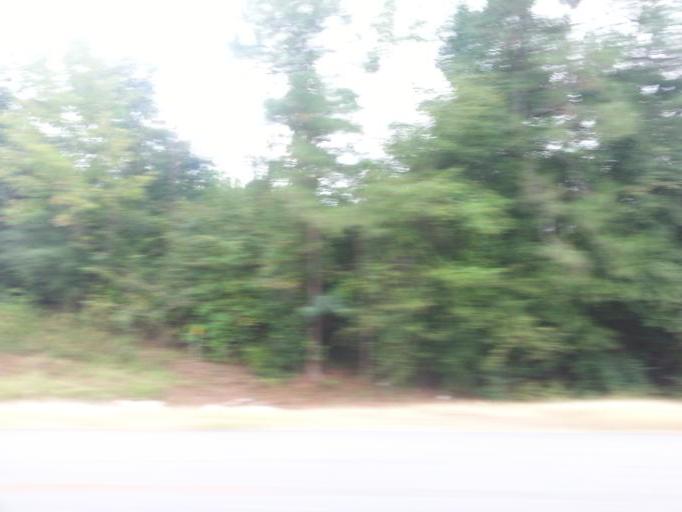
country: US
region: Alabama
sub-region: Conecuh County
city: Evergreen
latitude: 31.4378
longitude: -86.9844
